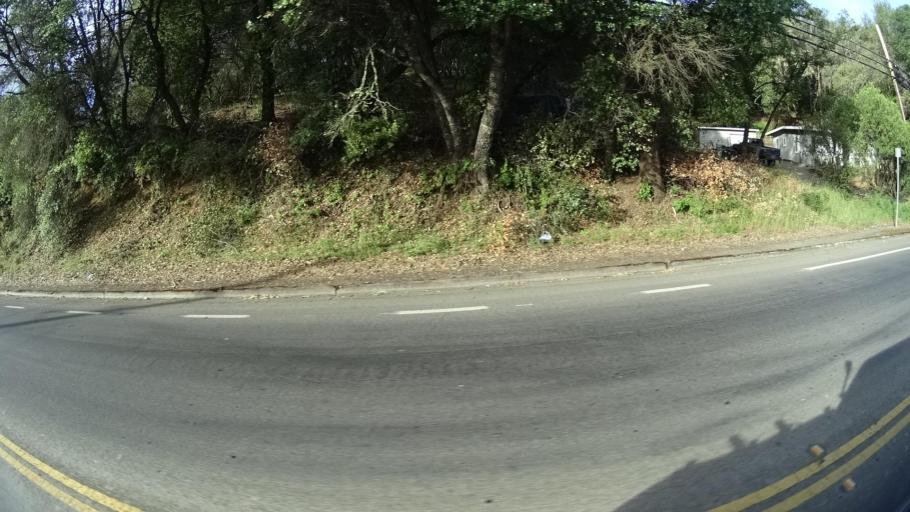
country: US
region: California
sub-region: Lake County
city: Lakeport
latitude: 39.0495
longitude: -122.9295
